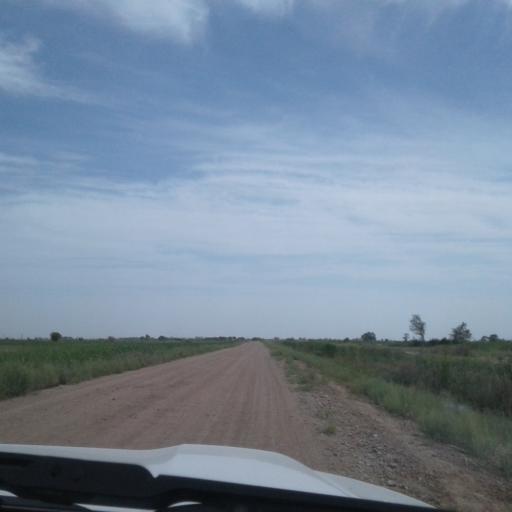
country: TM
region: Dasoguz
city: Tagta
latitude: 41.5427
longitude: 59.8090
